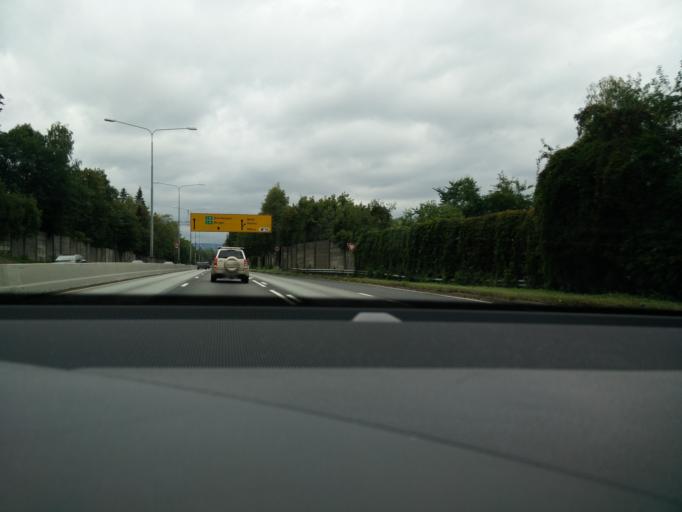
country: NO
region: Akershus
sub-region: Baerum
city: Lysaker
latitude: 59.9028
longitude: 10.5946
